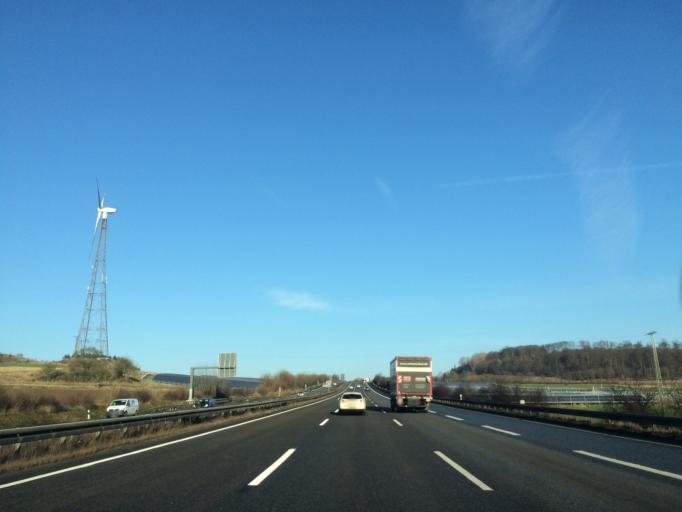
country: DE
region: Hesse
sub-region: Regierungsbezirk Kassel
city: Malsfeld
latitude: 51.0901
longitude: 9.4841
